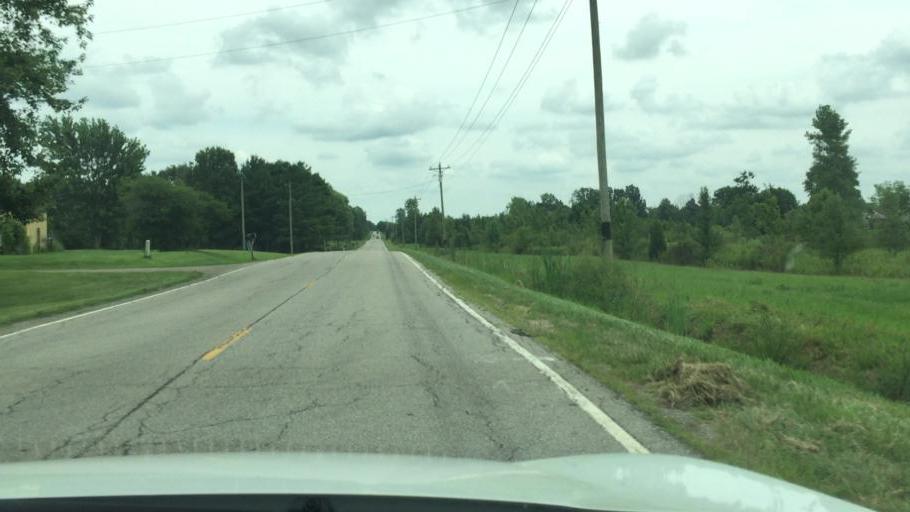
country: US
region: Ohio
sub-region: Champaign County
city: North Lewisburg
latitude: 40.2518
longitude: -83.4856
